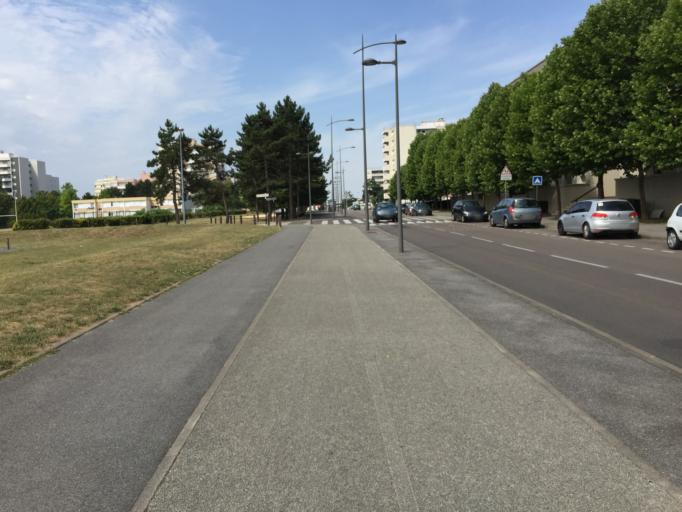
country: FR
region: Ile-de-France
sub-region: Departement de Seine-et-Marne
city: Fublaines
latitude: 48.9511
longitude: 2.9185
